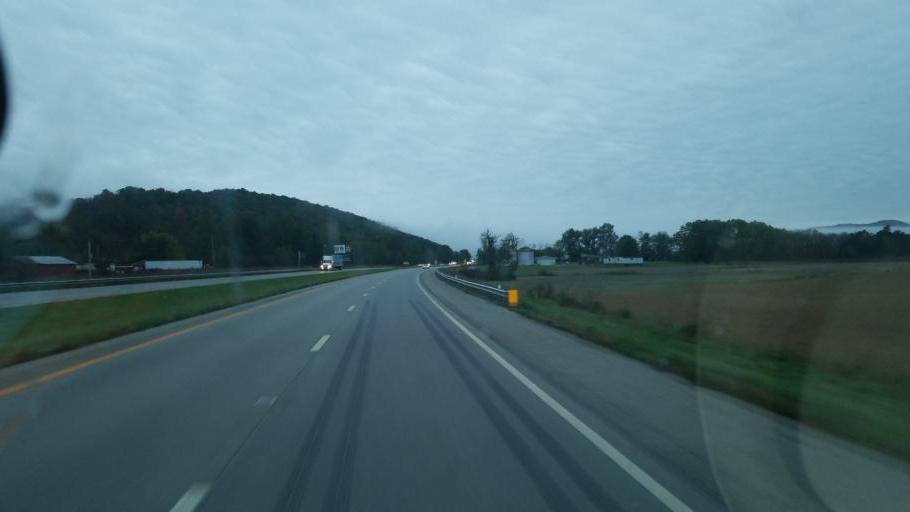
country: US
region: Ohio
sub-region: Pike County
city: Piketon
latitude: 38.9745
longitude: -83.0224
